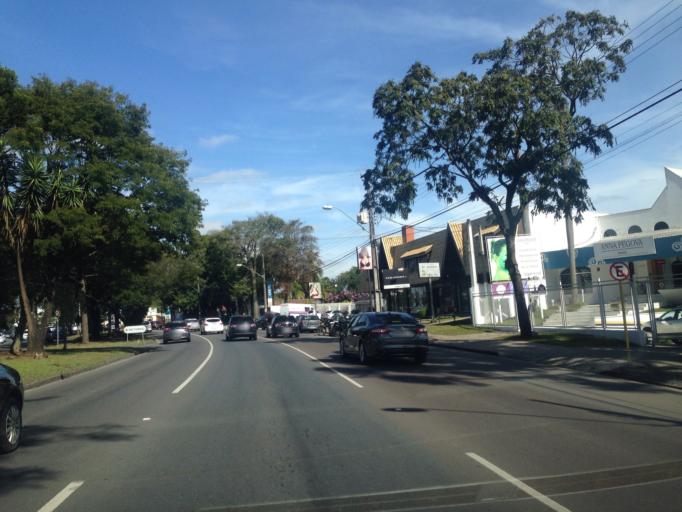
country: BR
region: Parana
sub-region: Curitiba
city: Curitiba
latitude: -25.4236
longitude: -49.2421
